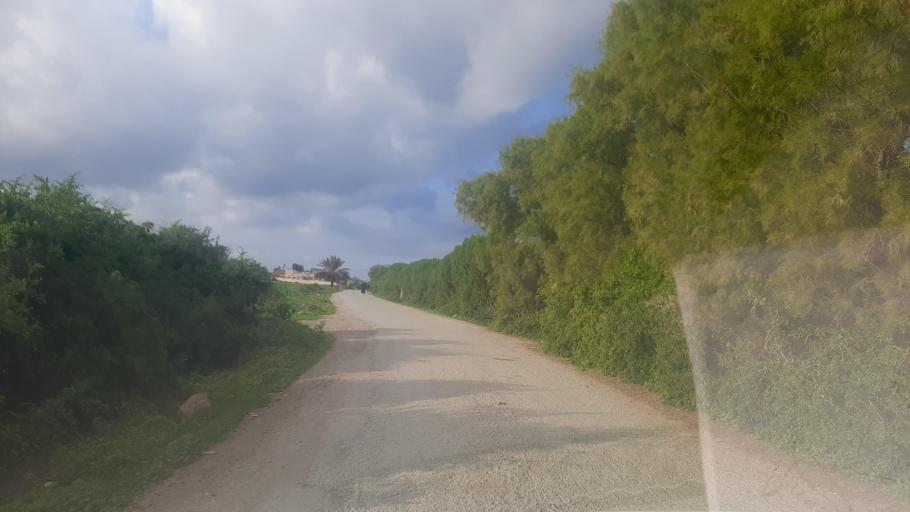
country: TN
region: Nabul
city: Manzil Bu Zalafah
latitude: 36.7130
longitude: 10.4992
